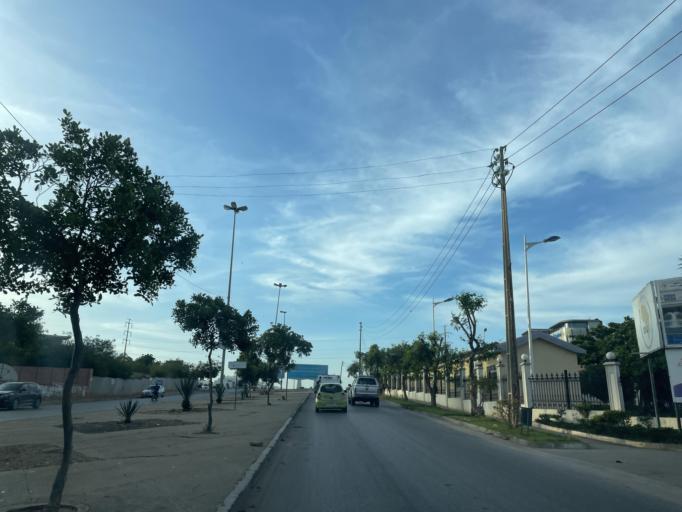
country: AO
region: Luanda
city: Luanda
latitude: -8.9224
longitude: 13.1929
